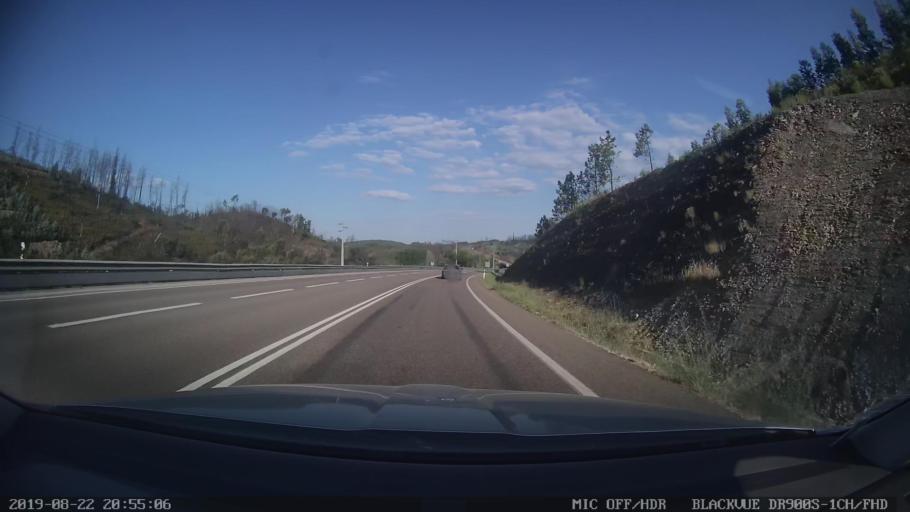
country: PT
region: Castelo Branco
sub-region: Serta
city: Serta
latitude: 39.7787
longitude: -8.0258
